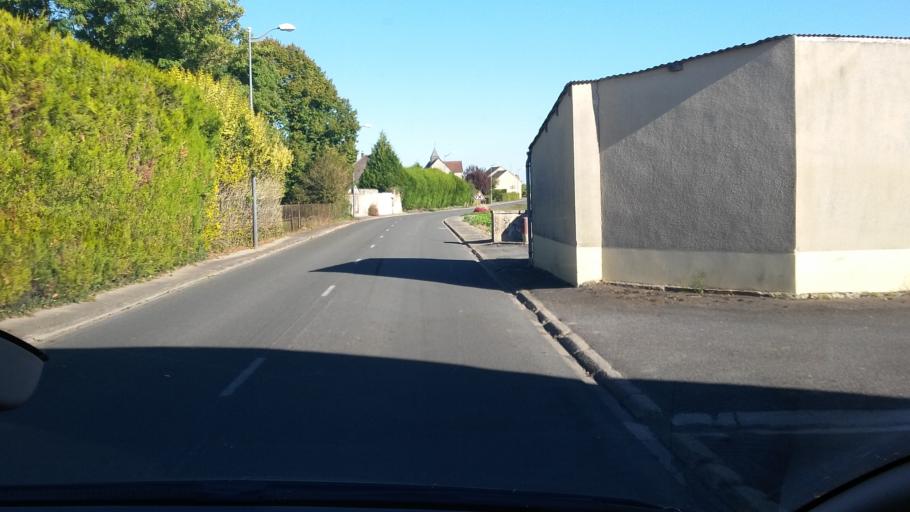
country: FR
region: Champagne-Ardenne
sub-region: Departement de la Marne
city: Fere-Champenoise
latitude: 48.8285
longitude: 3.9325
